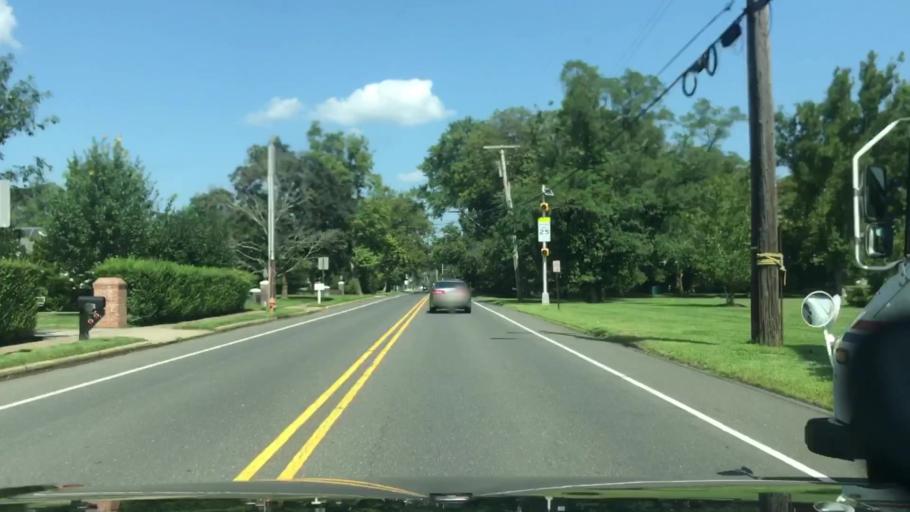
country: US
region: New Jersey
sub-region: Monmouth County
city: Little Silver
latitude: 40.3344
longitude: -74.0280
